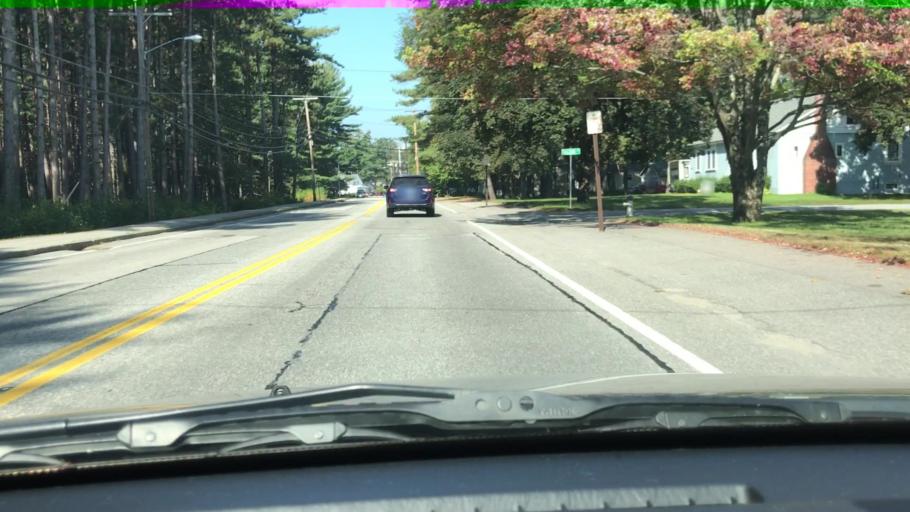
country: US
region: New Hampshire
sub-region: Cheshire County
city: Keene
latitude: 42.9411
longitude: -72.3085
